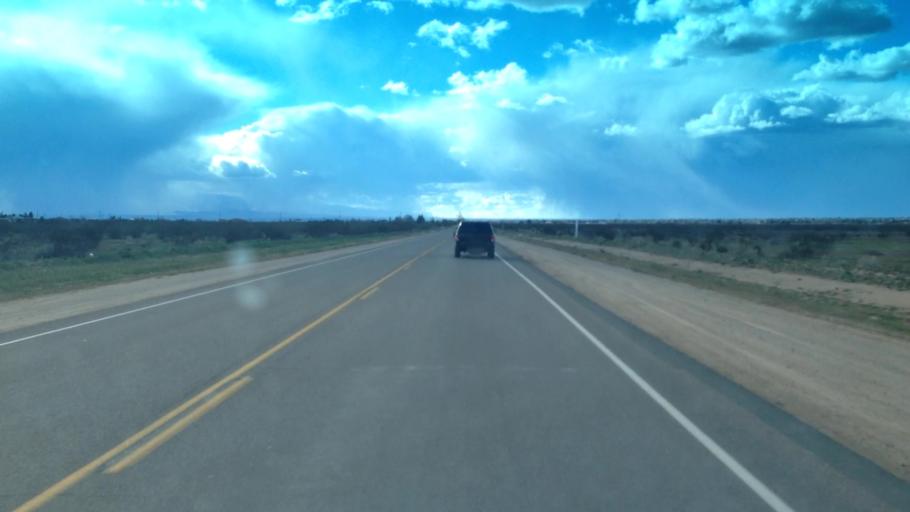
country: US
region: California
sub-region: San Bernardino County
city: Apple Valley
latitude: 34.4720
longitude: -117.1316
